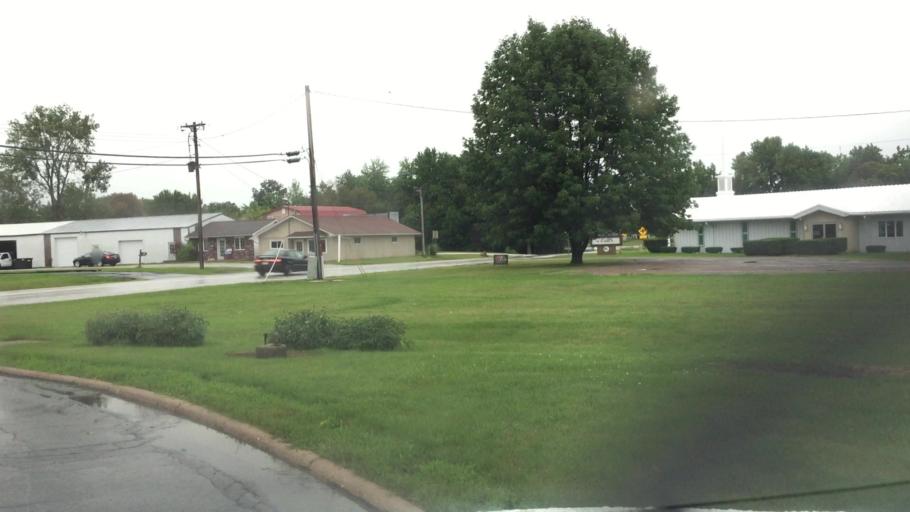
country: US
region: Illinois
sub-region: Hancock County
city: Carthage
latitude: 40.4216
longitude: -91.1359
